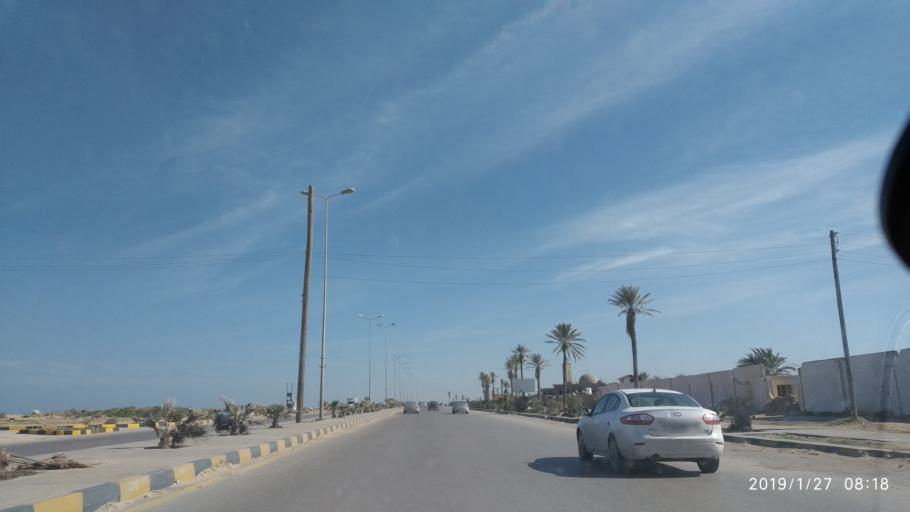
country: LY
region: Tripoli
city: Tagiura
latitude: 32.8951
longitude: 13.3337
